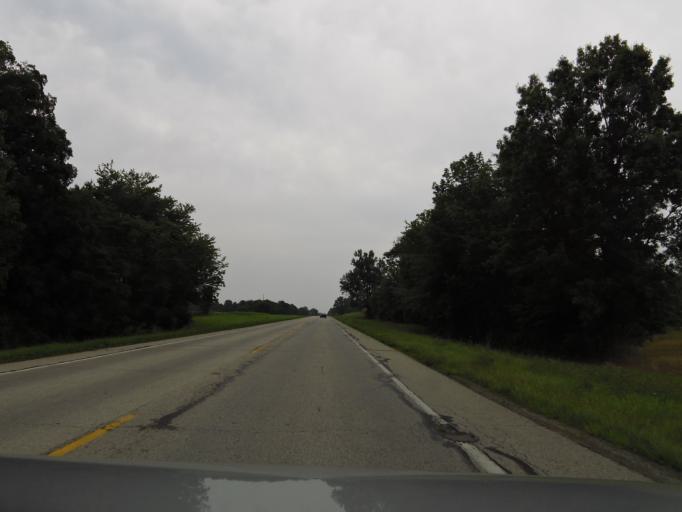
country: US
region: Ohio
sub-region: Brown County
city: Ripley
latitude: 38.8230
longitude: -83.8210
